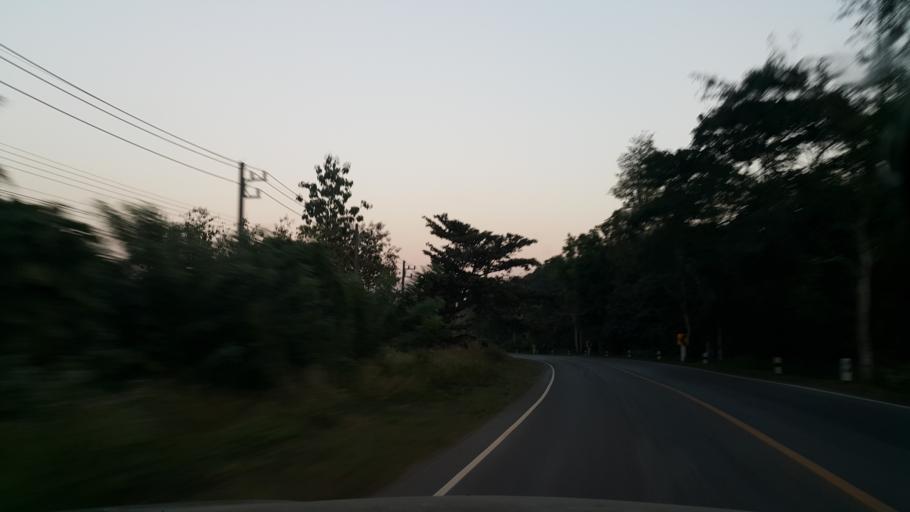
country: TH
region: Phrae
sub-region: Amphoe Wang Chin
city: Wang Chin
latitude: 17.9732
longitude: 99.6287
